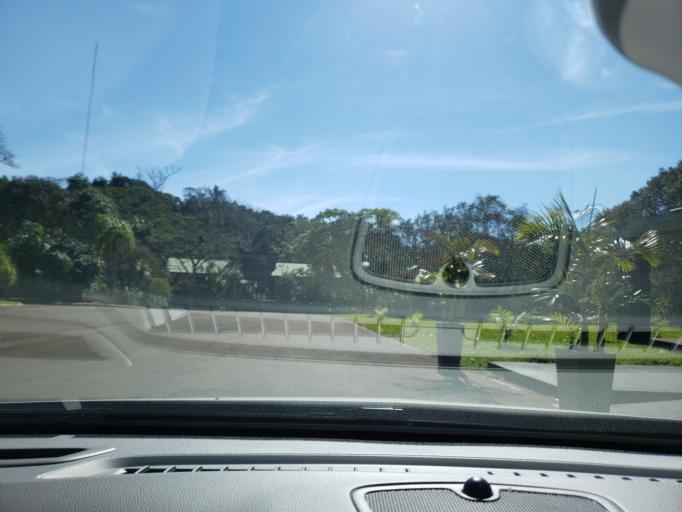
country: BR
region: Rio Grande do Sul
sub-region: Tres Passos
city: Tres Passos
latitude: -27.1537
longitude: -53.9013
